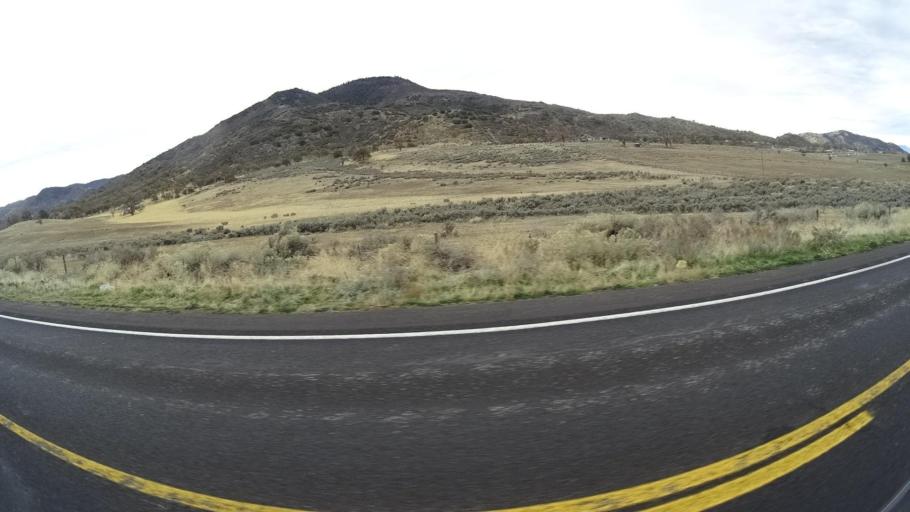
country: US
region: California
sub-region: Kern County
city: Stallion Springs
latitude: 35.0949
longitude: -118.5921
